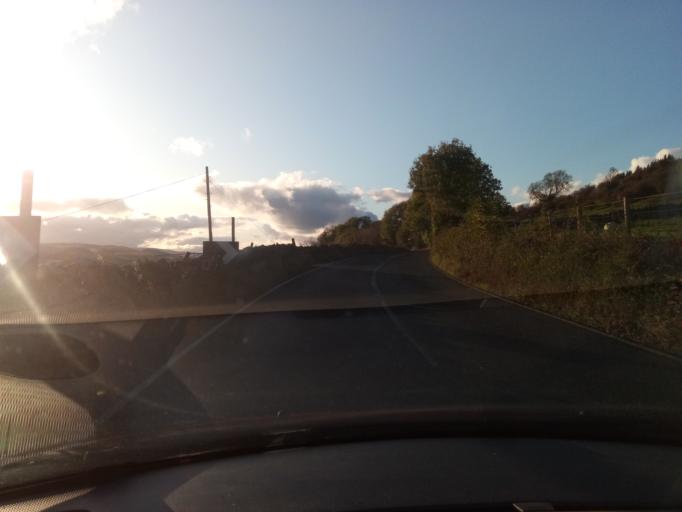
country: GB
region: England
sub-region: County Durham
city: Stanhope
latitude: 54.7458
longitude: -2.0370
